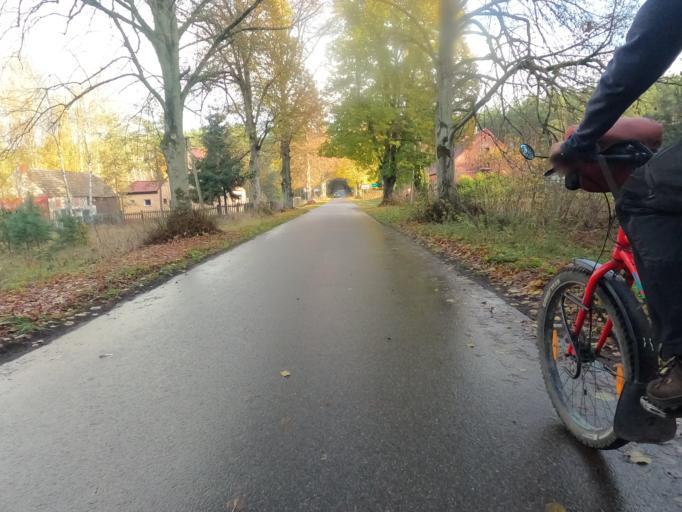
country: PL
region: West Pomeranian Voivodeship
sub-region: Powiat szczecinecki
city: Borne Sulinowo
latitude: 53.5309
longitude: 16.4733
